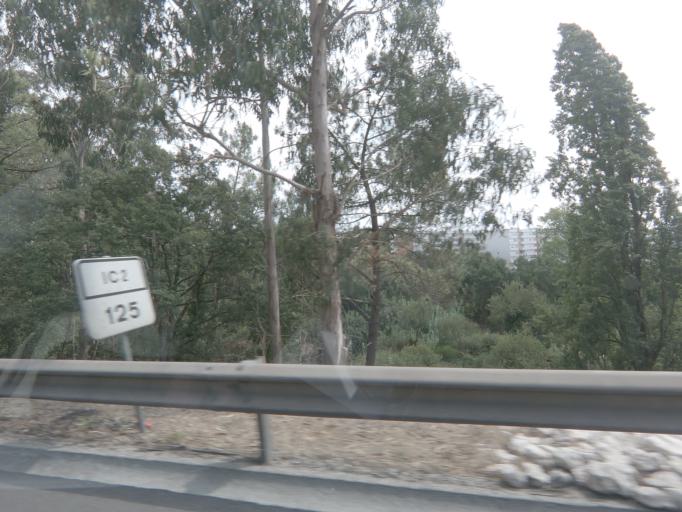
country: PT
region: Leiria
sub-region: Leiria
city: Leiria
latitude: 39.7609
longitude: -8.8028
